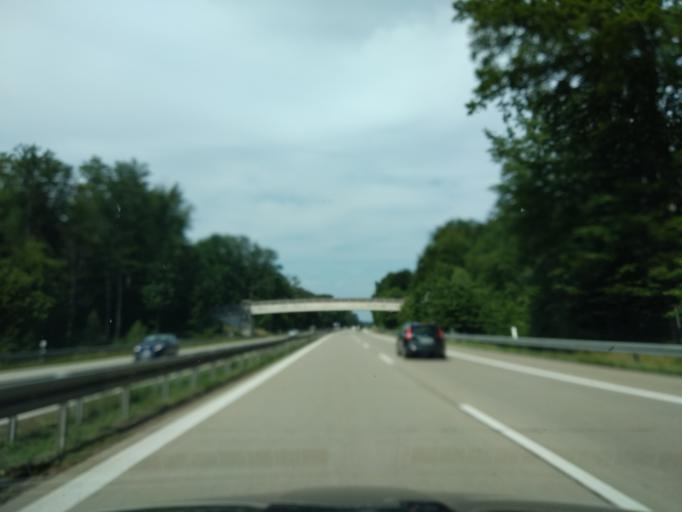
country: DE
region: Brandenburg
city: Gerswalde
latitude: 53.1099
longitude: 13.8593
